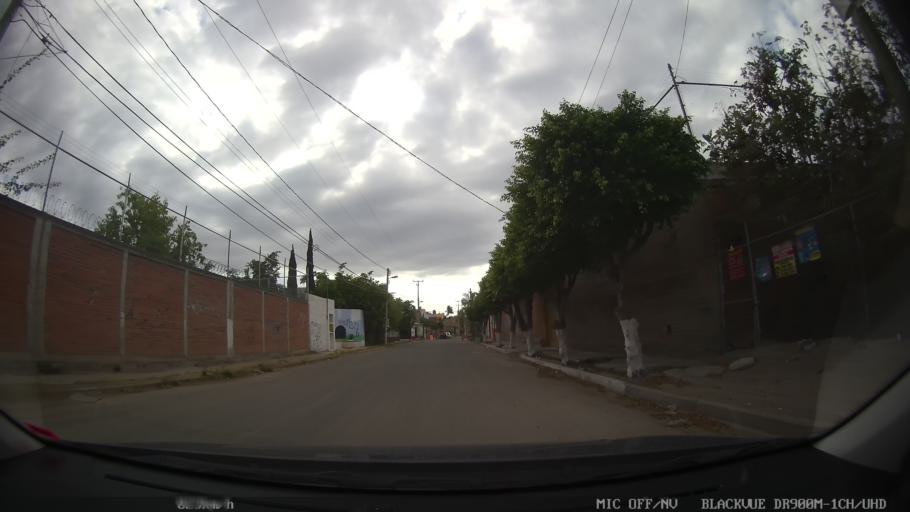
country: MX
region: Jalisco
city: Tonala
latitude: 20.6641
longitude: -103.2373
